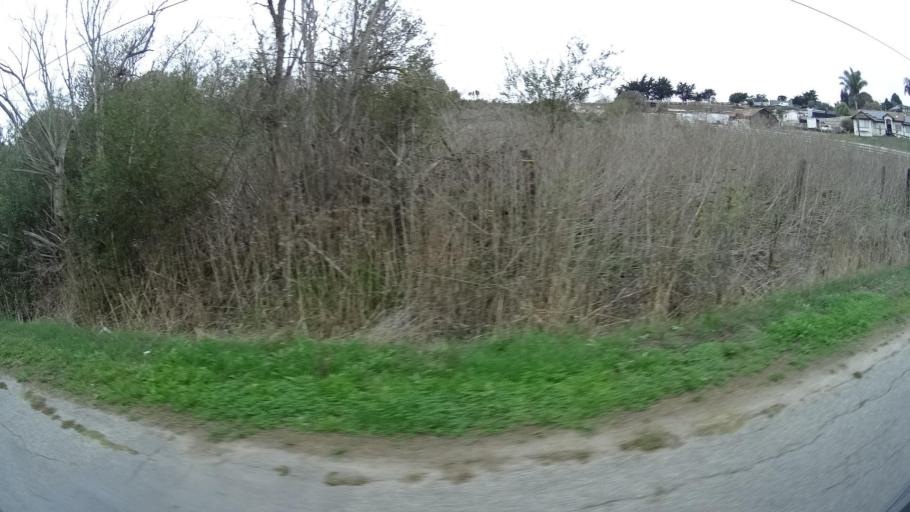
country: US
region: California
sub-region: Monterey County
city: Las Lomas
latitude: 36.8647
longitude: -121.7525
